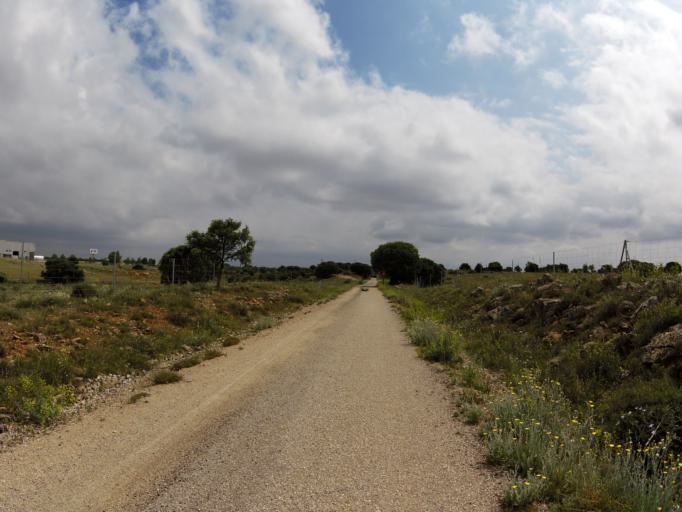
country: ES
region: Castille-La Mancha
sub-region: Provincia de Albacete
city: Robledo
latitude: 38.7671
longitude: -2.4542
